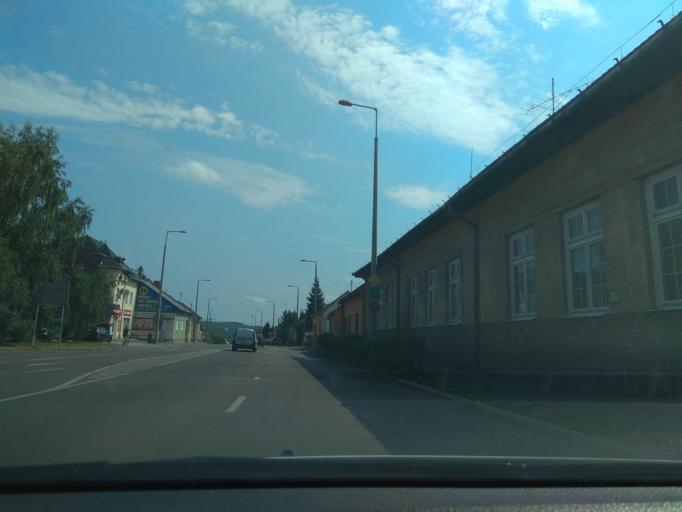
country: HU
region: Heves
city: Eger
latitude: 47.8929
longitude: 20.3719
